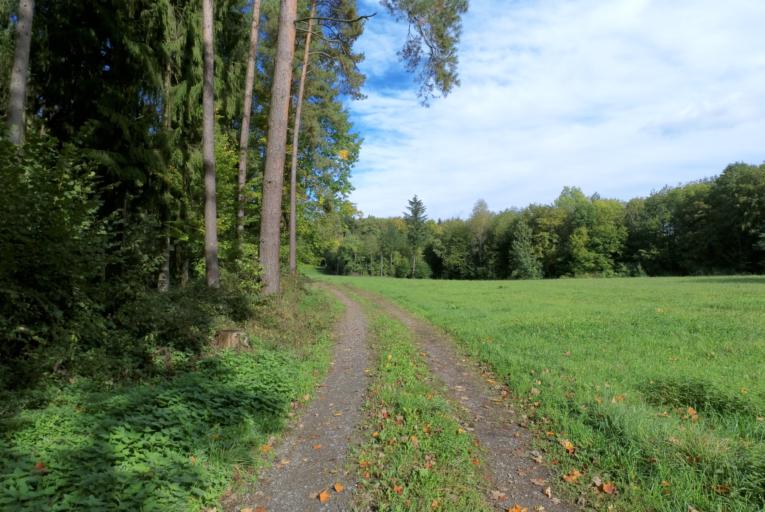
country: DE
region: Baden-Wuerttemberg
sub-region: Karlsruhe Region
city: Aglasterhausen
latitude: 49.3431
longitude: 8.9875
